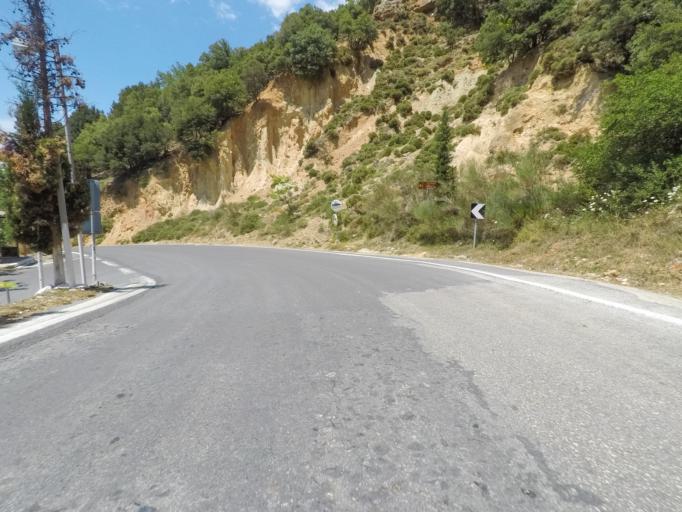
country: GR
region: Crete
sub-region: Nomos Irakleiou
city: Mokhos
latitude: 35.2248
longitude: 25.4631
